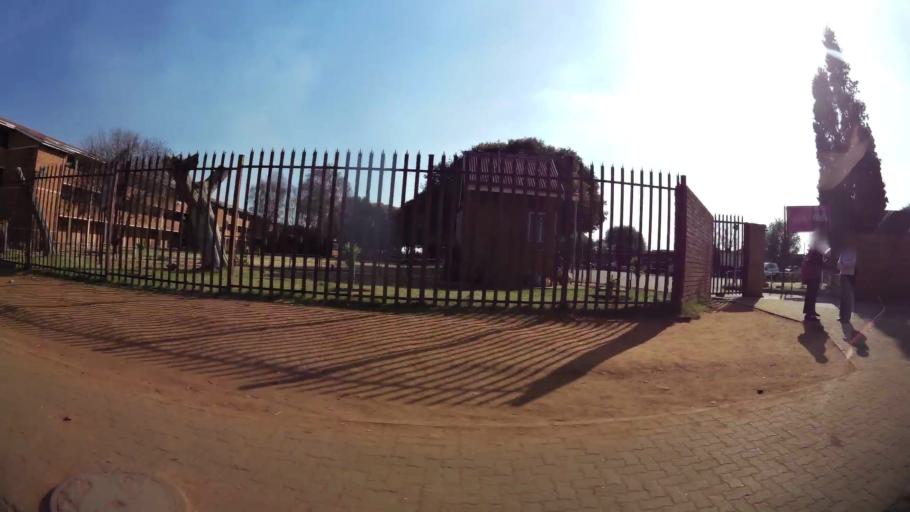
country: ZA
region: Gauteng
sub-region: Ekurhuleni Metropolitan Municipality
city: Benoni
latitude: -26.1549
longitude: 28.4005
